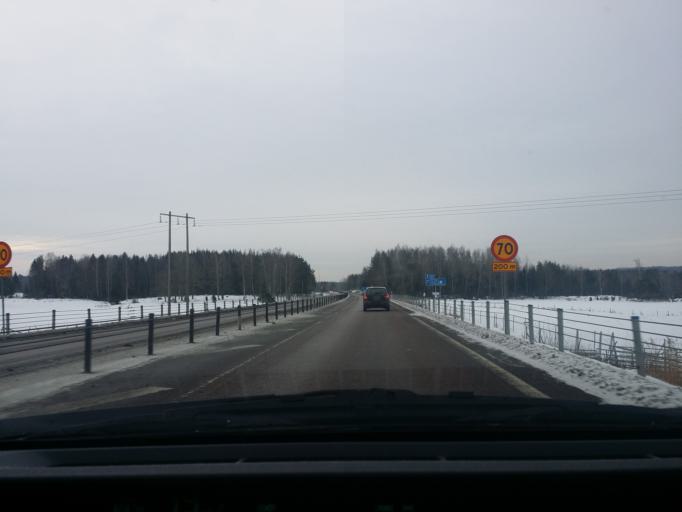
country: SE
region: Vaestra Goetaland
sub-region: Skovde Kommun
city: Stopen
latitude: 58.5319
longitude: 13.8160
